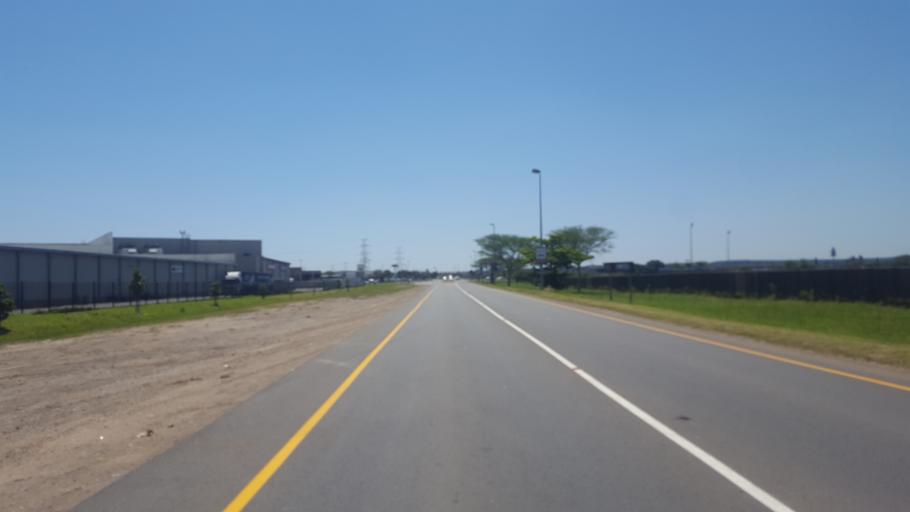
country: ZA
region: KwaZulu-Natal
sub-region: uThungulu District Municipality
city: Richards Bay
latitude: -28.7471
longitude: 32.0528
